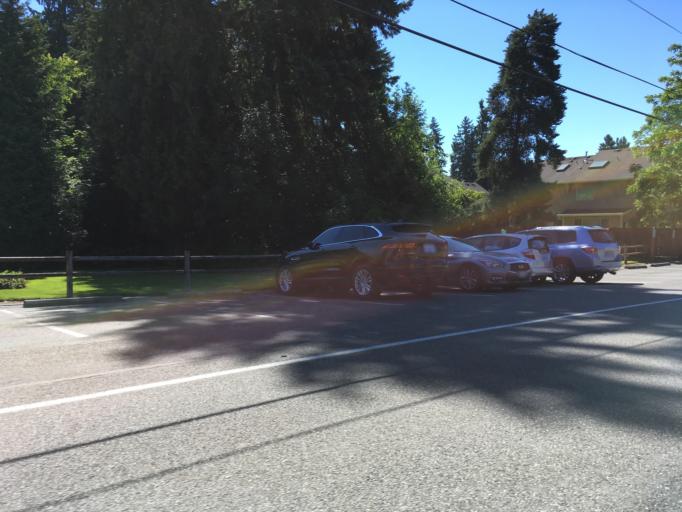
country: US
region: Washington
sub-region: King County
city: Bellevue
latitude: 47.6241
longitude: -122.1963
